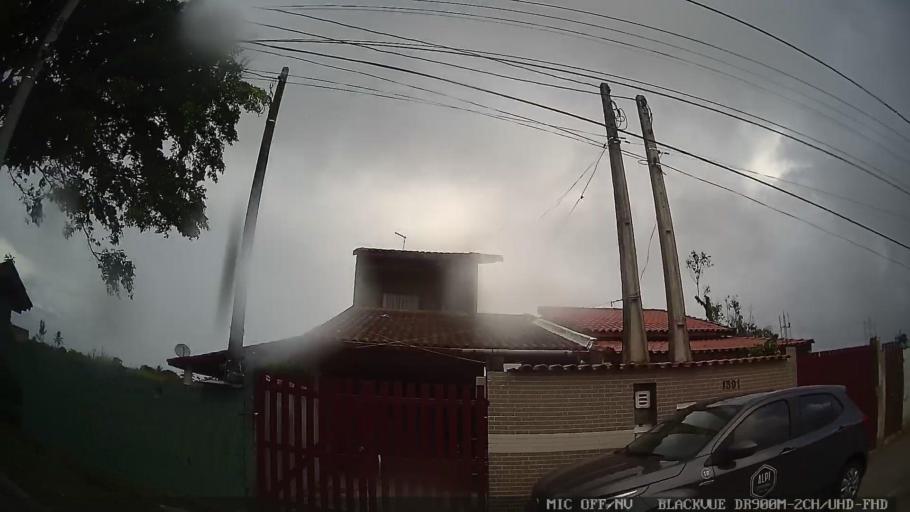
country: BR
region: Sao Paulo
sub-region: Itanhaem
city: Itanhaem
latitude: -24.2144
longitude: -46.8649
